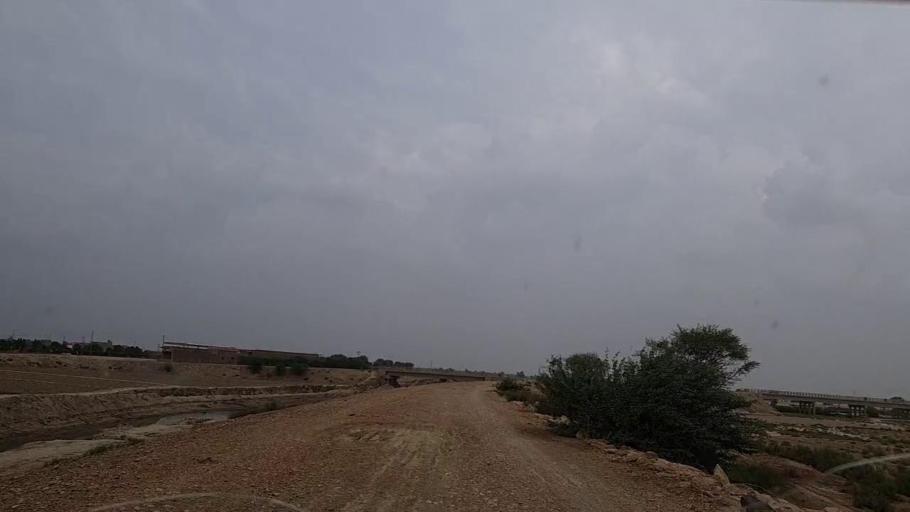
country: PK
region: Sindh
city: Johi
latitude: 26.6996
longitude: 67.5988
